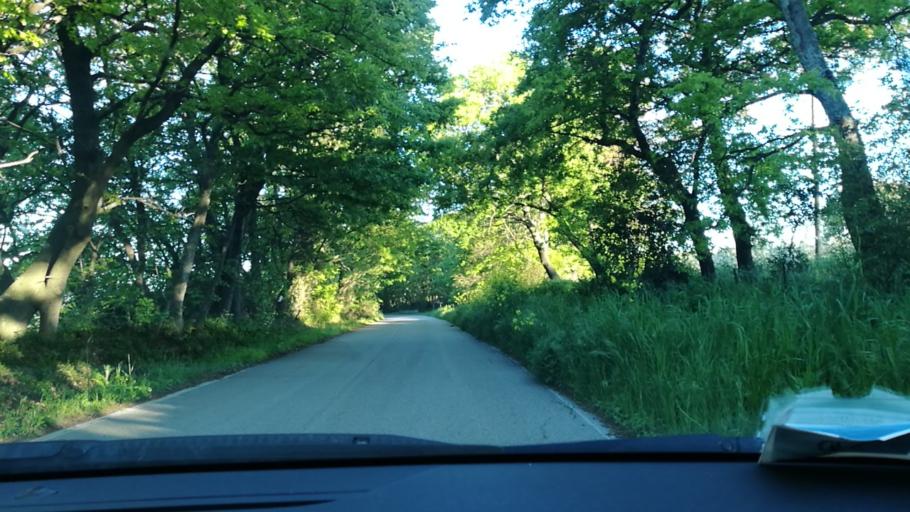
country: IT
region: Molise
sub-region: Provincia di Campobasso
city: Petacciato
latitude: 42.0045
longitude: 14.8814
